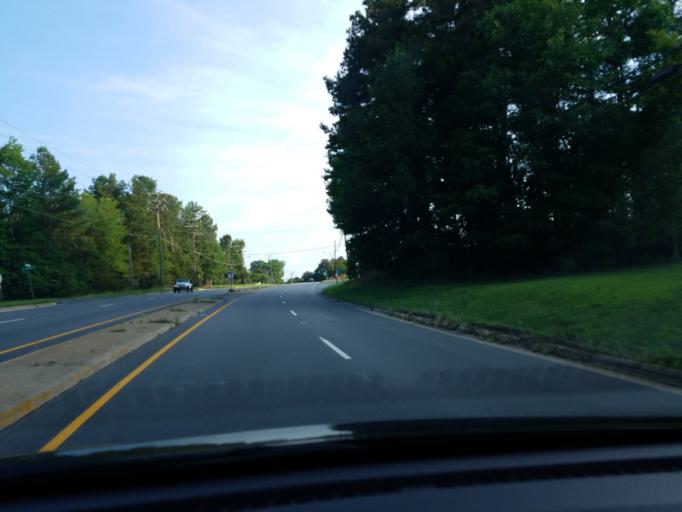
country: US
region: North Carolina
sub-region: Durham County
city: Durham
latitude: 36.0961
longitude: -78.9099
